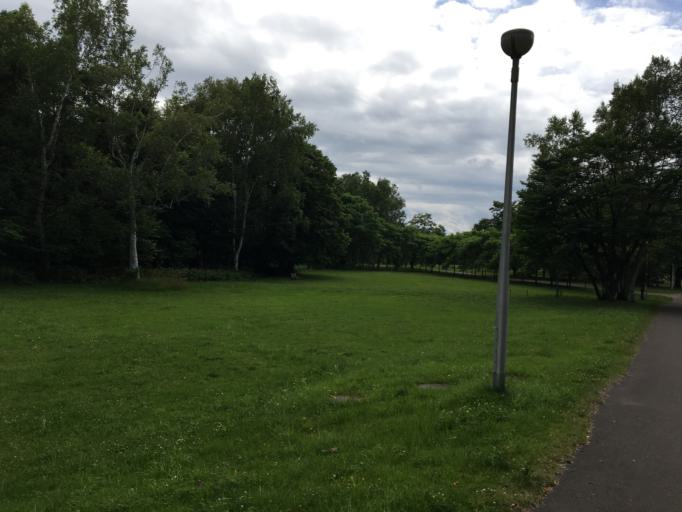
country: JP
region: Hokkaido
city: Sapporo
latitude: 42.9952
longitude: 141.3453
